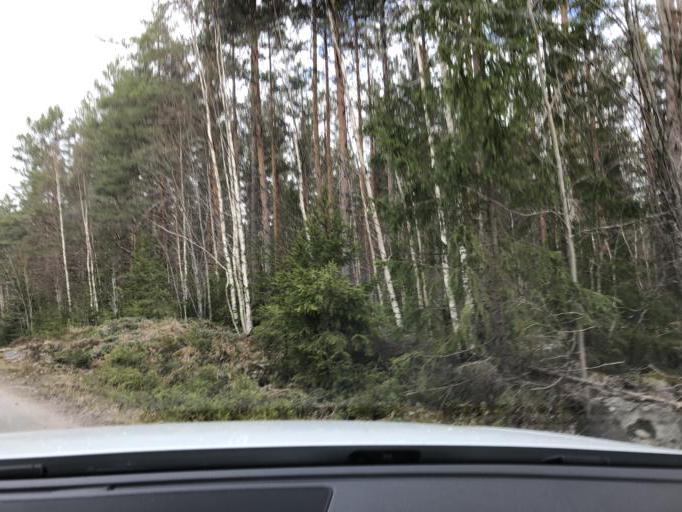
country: SE
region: Gaevleborg
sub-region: Gavle Kommun
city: Hedesunda
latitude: 60.3206
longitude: 17.1002
